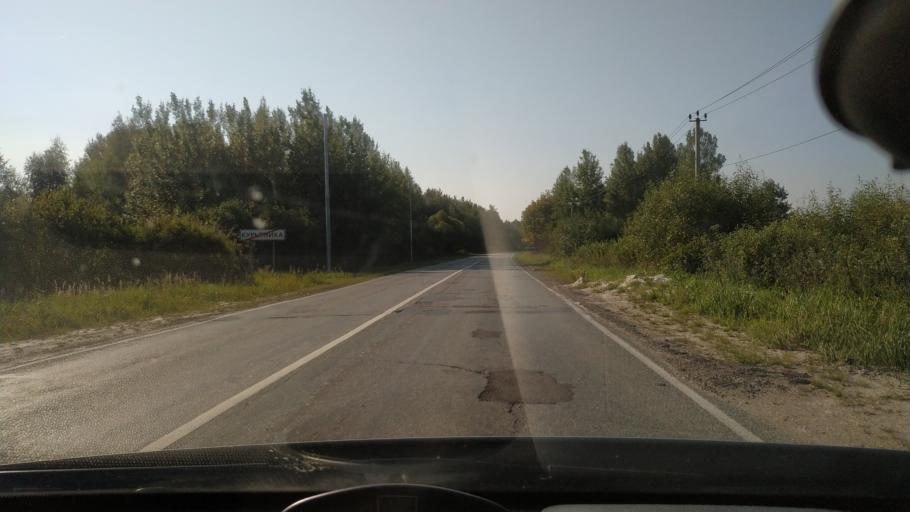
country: RU
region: Moskovskaya
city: Tugolesskiy Bor
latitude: 55.5340
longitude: 39.7084
